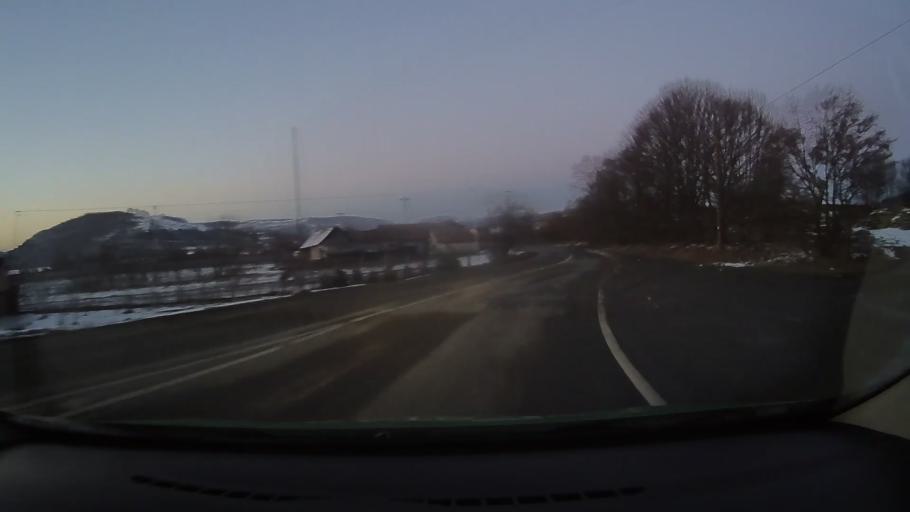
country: RO
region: Sibiu
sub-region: Comuna Alma
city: Alma
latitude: 46.1944
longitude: 24.4711
